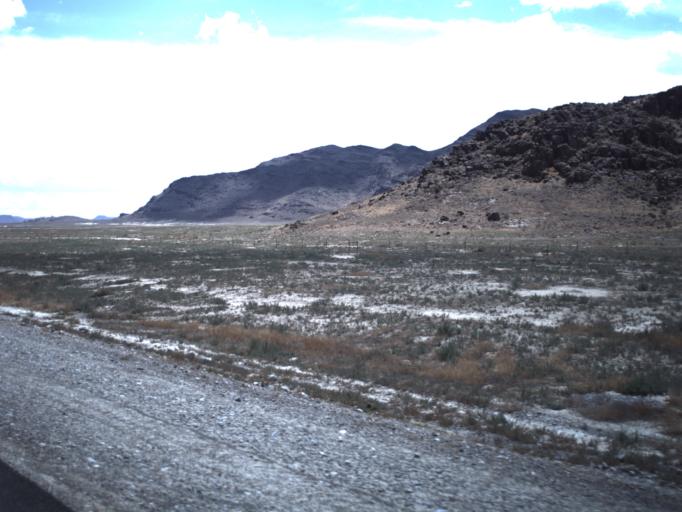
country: US
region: Utah
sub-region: Beaver County
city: Milford
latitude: 39.0578
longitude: -113.4331
